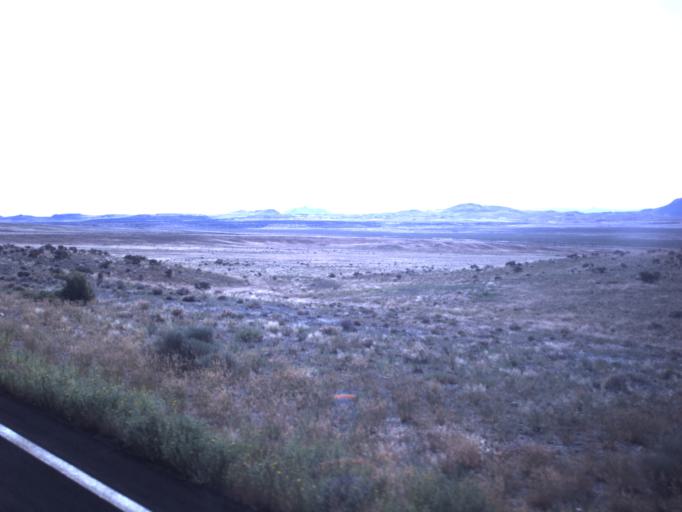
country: US
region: Utah
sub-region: Beaver County
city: Milford
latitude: 38.7911
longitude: -112.9094
